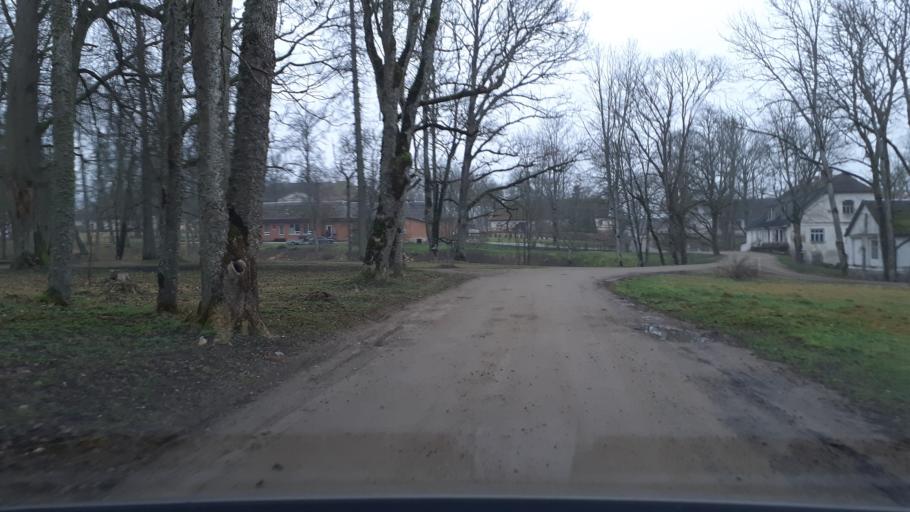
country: LV
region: Talsu Rajons
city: Sabile
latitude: 56.9522
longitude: 22.3996
